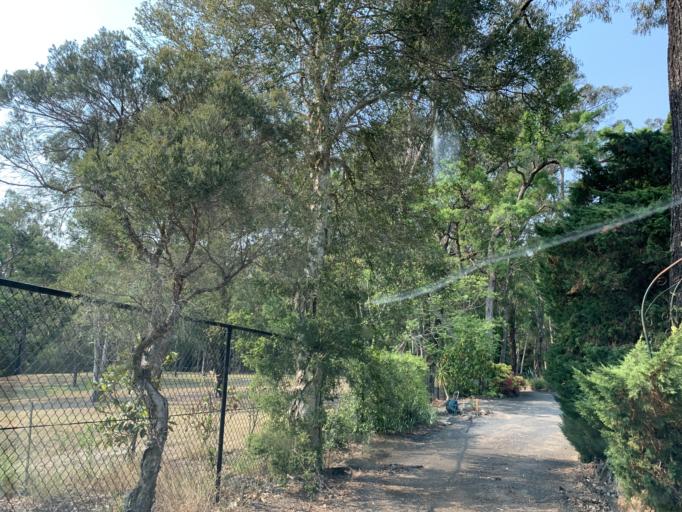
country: AU
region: New South Wales
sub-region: Blacktown
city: Rouse Hill
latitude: -33.6569
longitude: 150.9284
